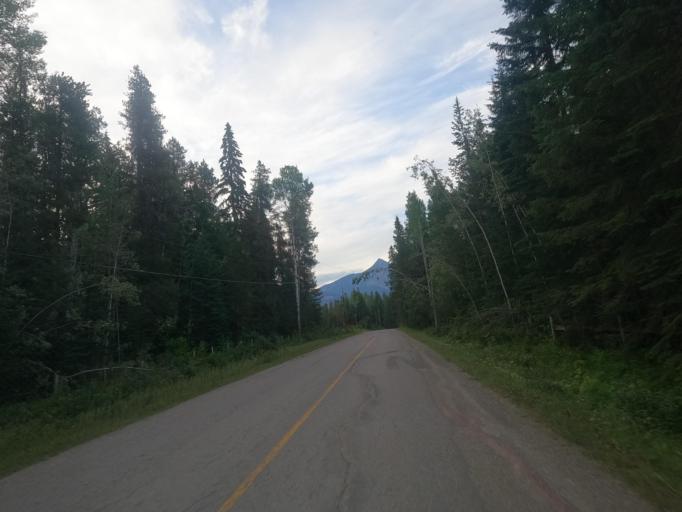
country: CA
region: British Columbia
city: Golden
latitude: 51.4326
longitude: -117.0491
